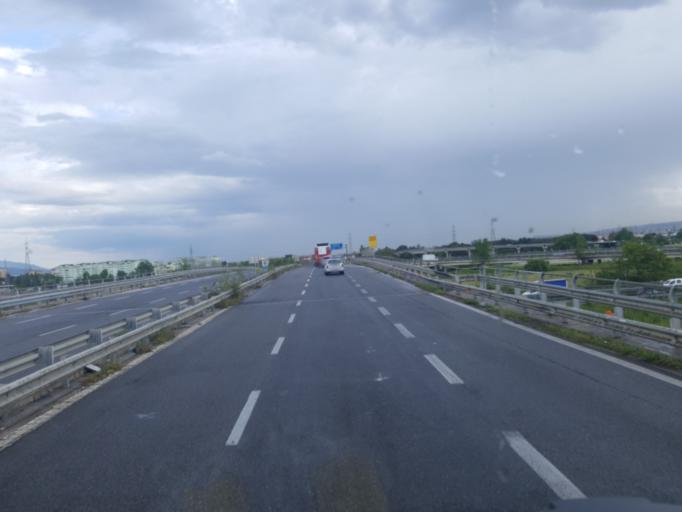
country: IT
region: Campania
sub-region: Provincia di Napoli
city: Pascarola
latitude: 40.9744
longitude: 14.2930
